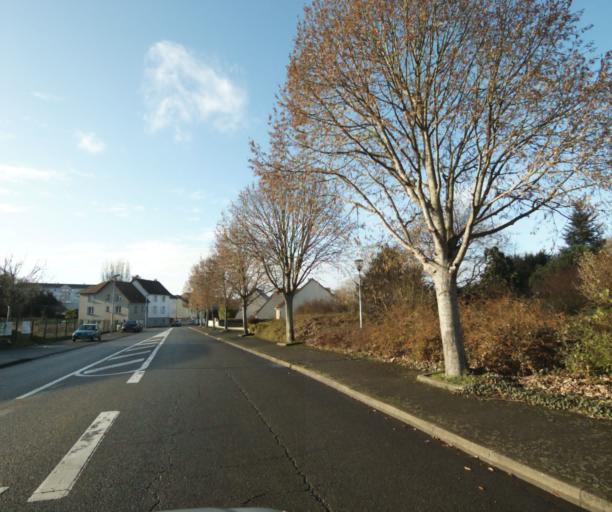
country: FR
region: Pays de la Loire
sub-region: Departement de la Sarthe
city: Coulaines
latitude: 48.0254
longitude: 0.2109
